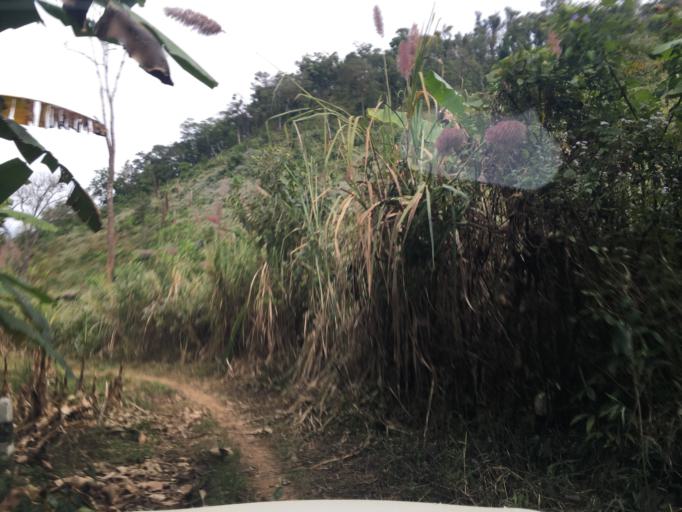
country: LA
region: Houaphan
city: Viengthong
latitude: 19.9136
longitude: 103.2998
